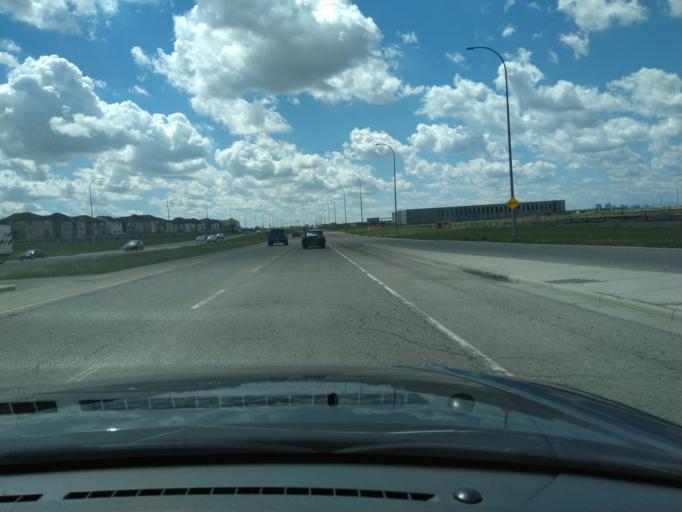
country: CA
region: Alberta
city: Calgary
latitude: 51.1536
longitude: -113.9703
